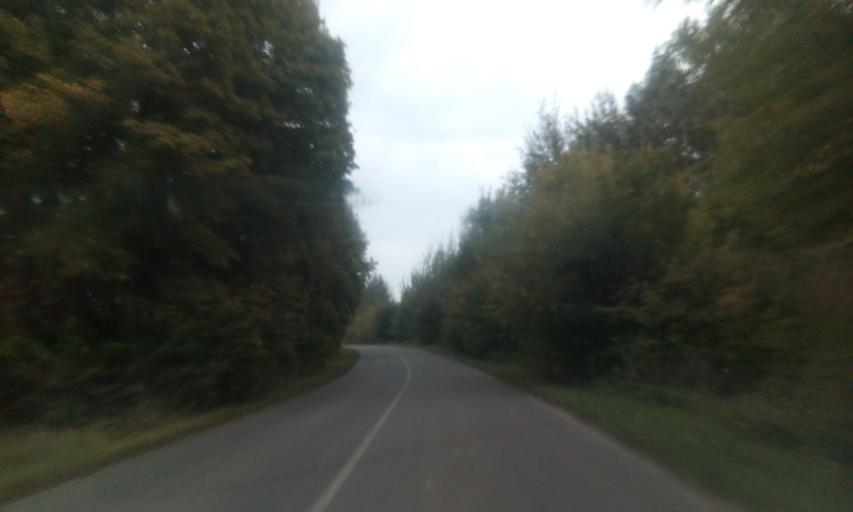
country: RU
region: Tula
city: Dubovka
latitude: 53.9566
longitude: 38.0634
